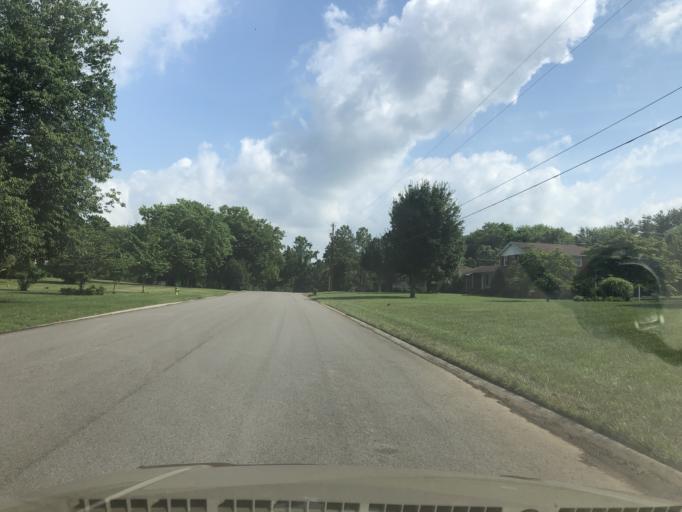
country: US
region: Tennessee
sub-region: Wilson County
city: Green Hill
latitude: 36.2346
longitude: -86.5862
